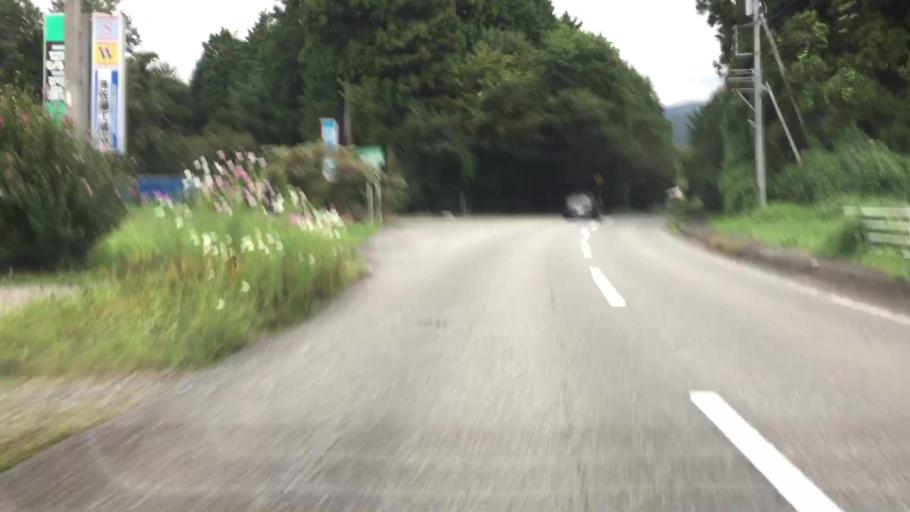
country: JP
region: Tochigi
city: Imaichi
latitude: 36.7707
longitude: 139.7056
